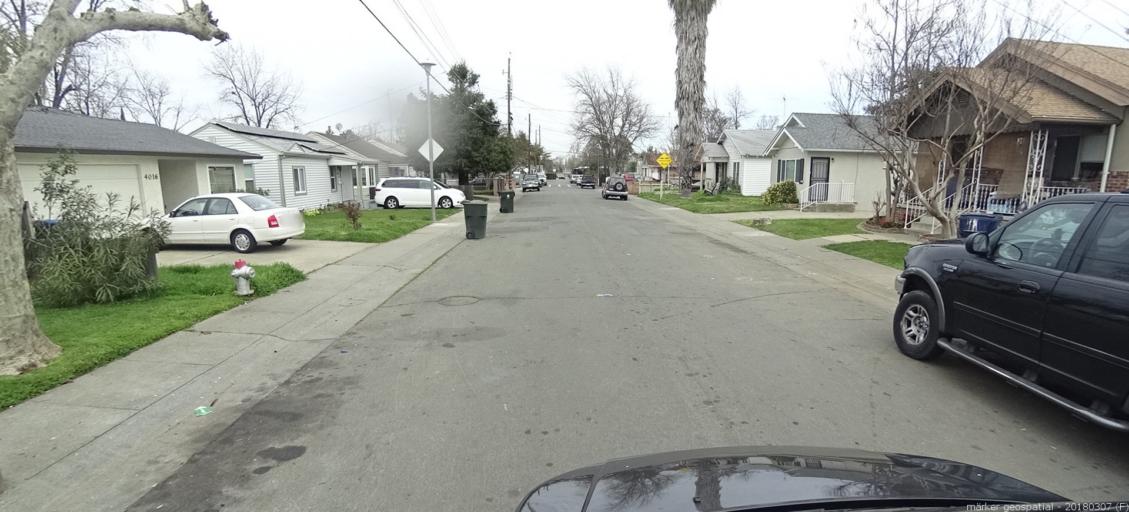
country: US
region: California
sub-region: Sacramento County
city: Parkway
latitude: 38.5381
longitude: -121.4618
